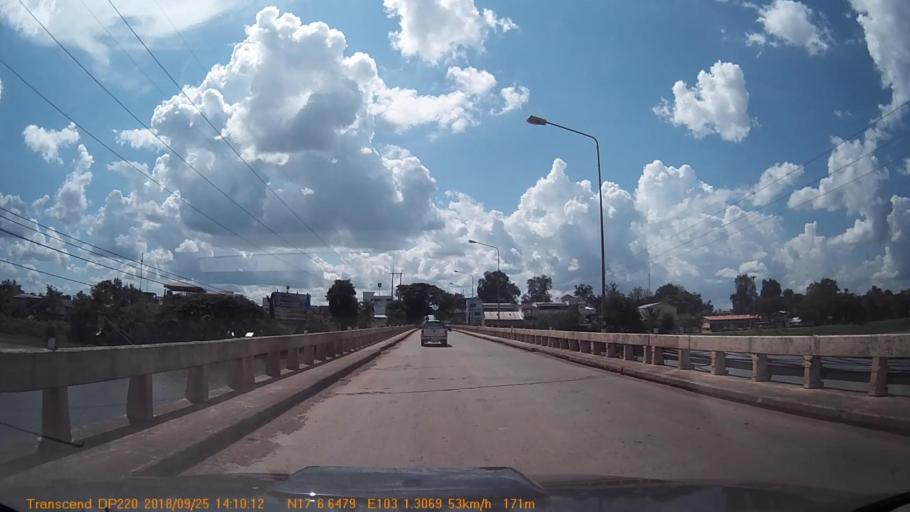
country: TH
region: Changwat Udon Thani
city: Kumphawapi
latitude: 17.1108
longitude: 103.0216
